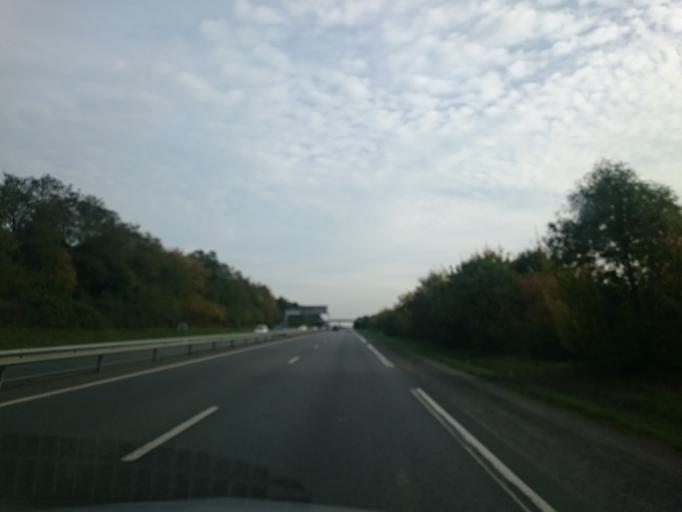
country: FR
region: Brittany
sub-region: Departement d'Ille-et-Vilaine
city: Vern-sur-Seiche
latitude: 48.0422
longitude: -1.6062
